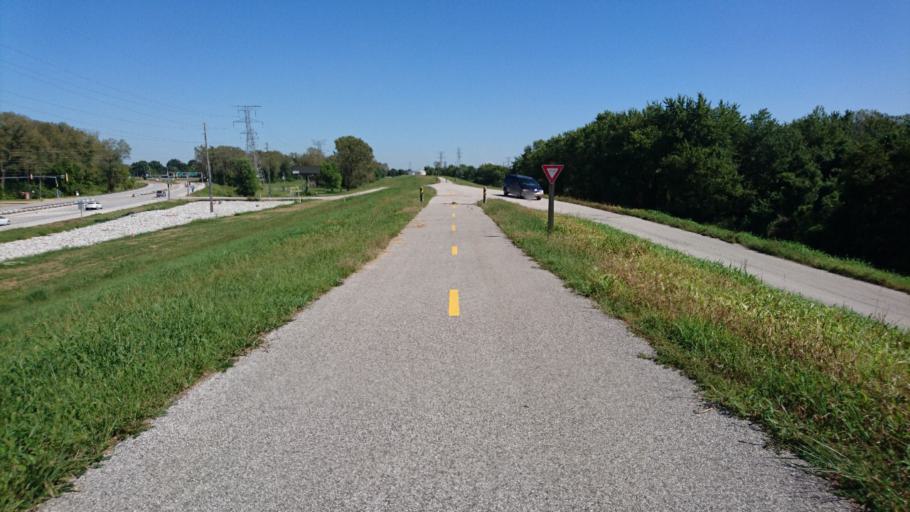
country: US
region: Illinois
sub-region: Madison County
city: Wood River
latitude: 38.8570
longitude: -90.1175
